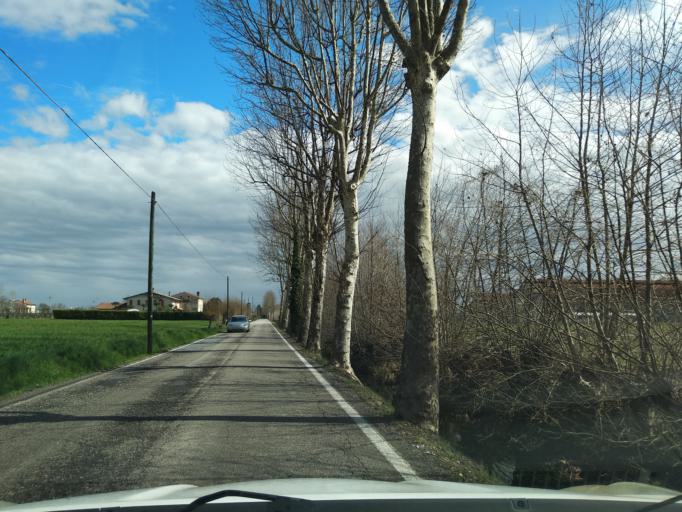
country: IT
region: Veneto
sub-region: Provincia di Vicenza
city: Vigardolo
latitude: 45.5996
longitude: 11.5910
